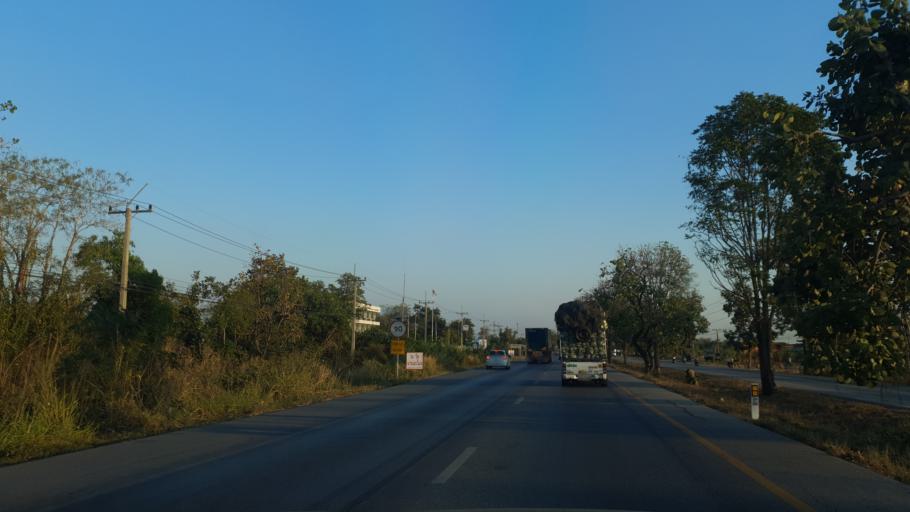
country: TH
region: Kamphaeng Phet
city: Khanu Woralaksaburi
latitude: 16.0245
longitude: 99.7790
